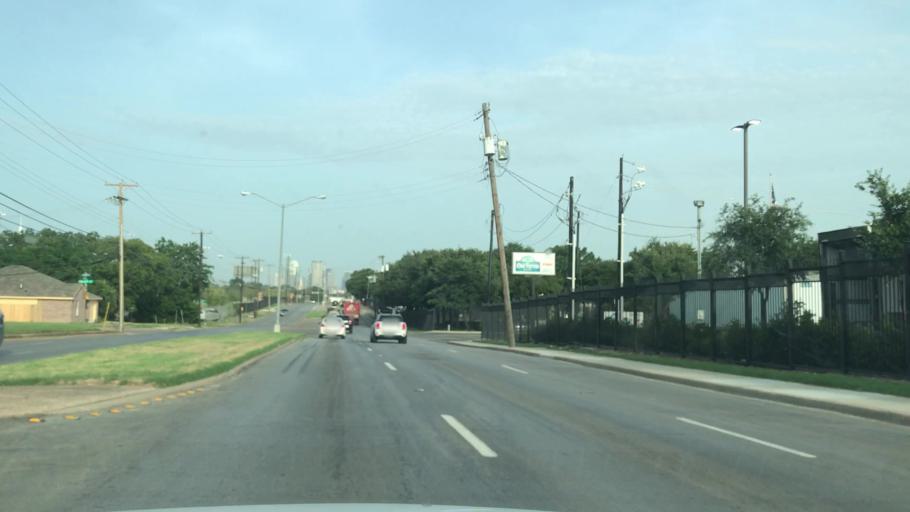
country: US
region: Texas
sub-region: Dallas County
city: Dallas
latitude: 32.7830
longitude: -96.7395
